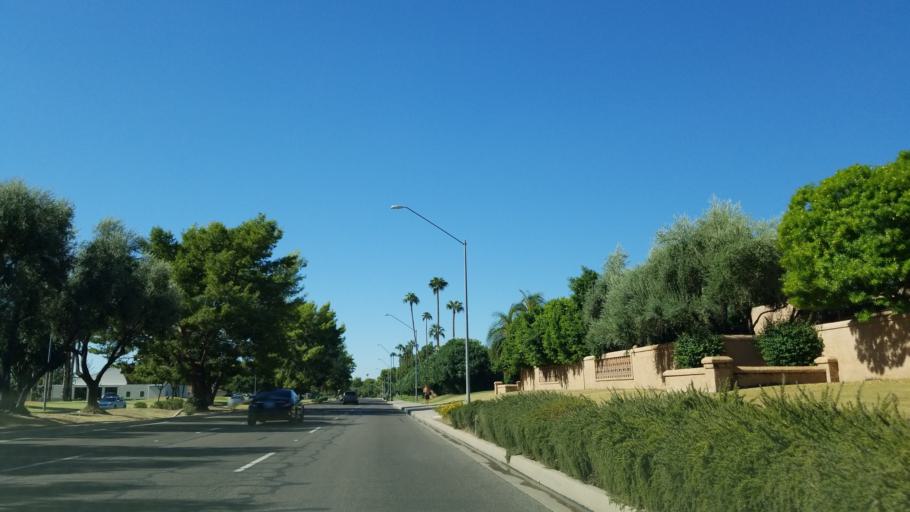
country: US
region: Arizona
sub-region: Maricopa County
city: Scottsdale
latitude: 33.5459
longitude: -111.9052
